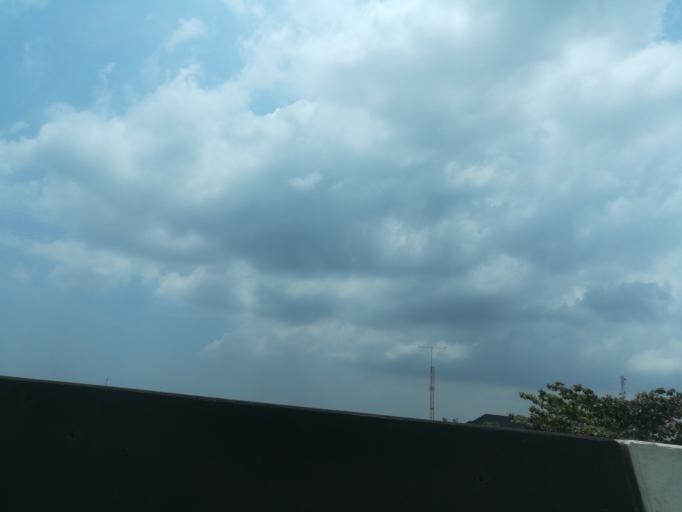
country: NG
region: Lagos
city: Ojota
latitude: 6.5949
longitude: 3.3636
